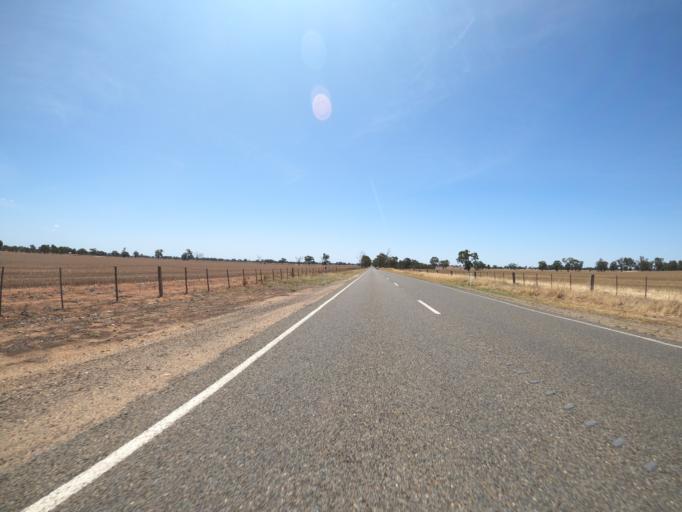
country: AU
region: Victoria
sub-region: Moira
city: Yarrawonga
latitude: -36.0741
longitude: 145.9954
